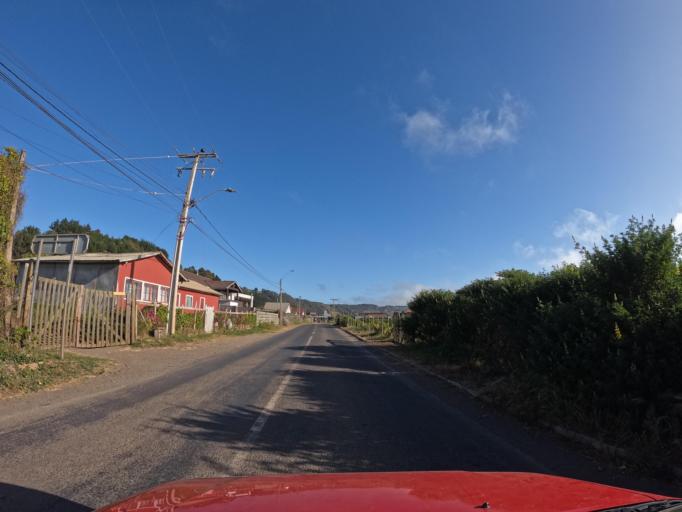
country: CL
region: Maule
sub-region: Provincia de Talca
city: Constitucion
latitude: -34.9226
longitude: -72.1797
